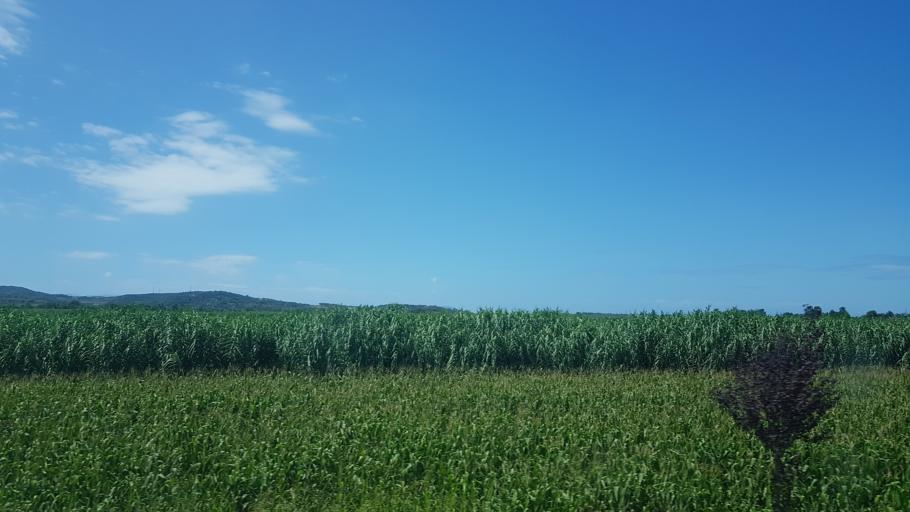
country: AL
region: Fier
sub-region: Rrethi i Fierit
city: Frakulla e Madhe
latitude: 40.6207
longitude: 19.5169
